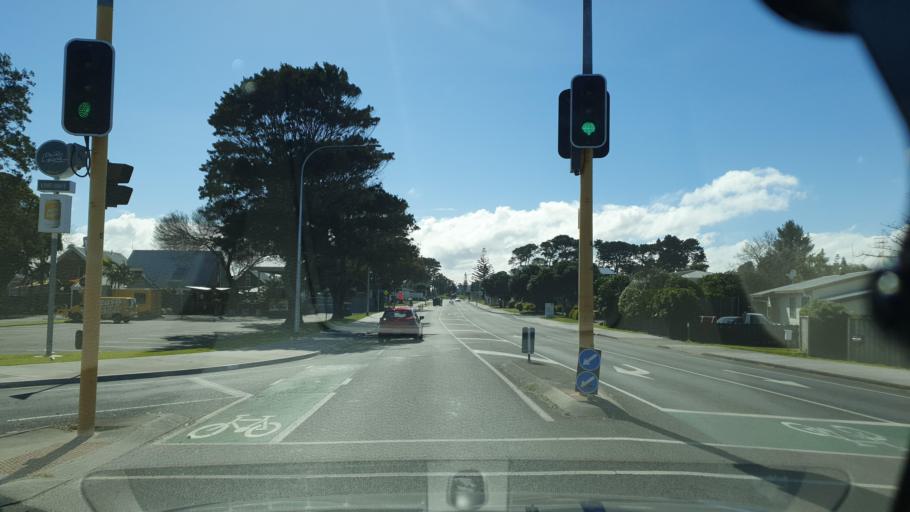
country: NZ
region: Bay of Plenty
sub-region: Tauranga City
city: Tauranga
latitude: -37.7008
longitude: 176.2848
